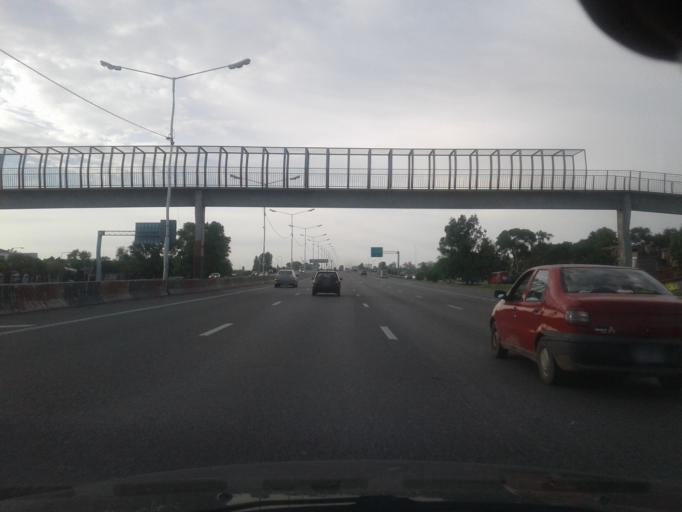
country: AR
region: Santa Fe
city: Perez
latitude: -32.9355
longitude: -60.7229
